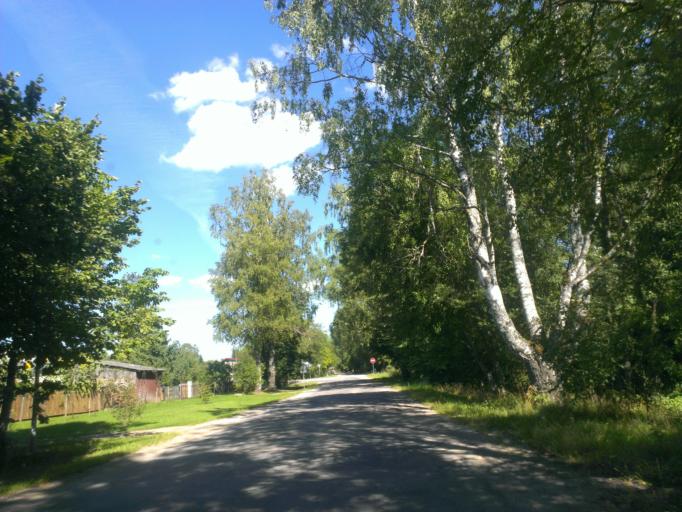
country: LV
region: Malpils
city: Malpils
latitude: 57.0077
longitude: 24.9650
